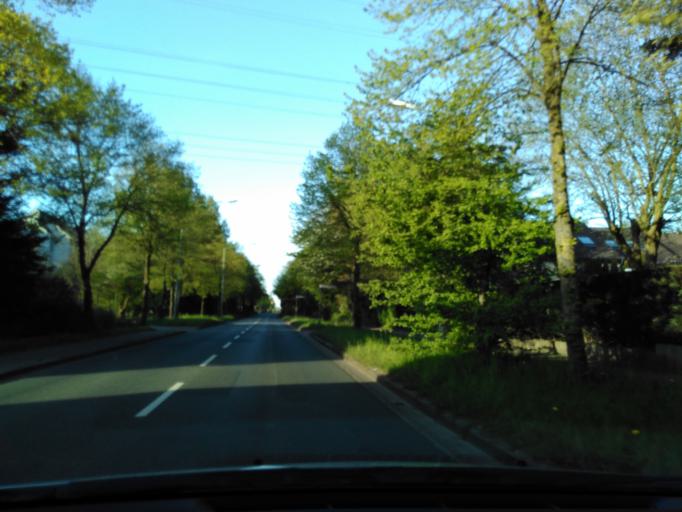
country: DE
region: Lower Saxony
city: Osnabrueck
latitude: 52.2583
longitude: 7.9964
